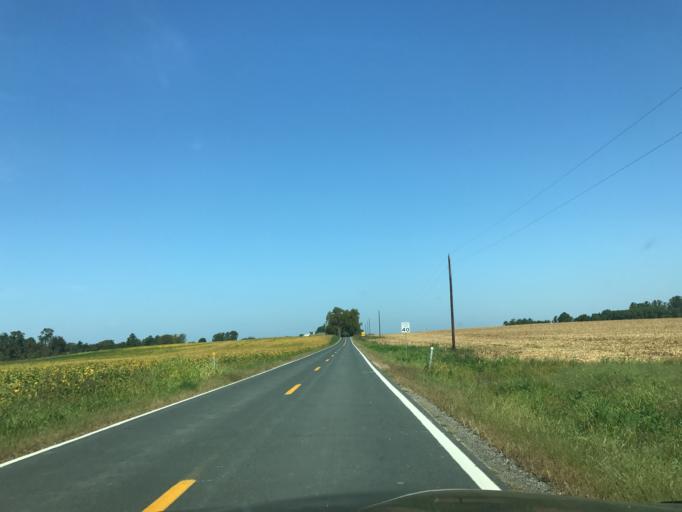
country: US
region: Maryland
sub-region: Queen Anne's County
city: Kingstown
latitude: 39.3546
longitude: -75.9632
